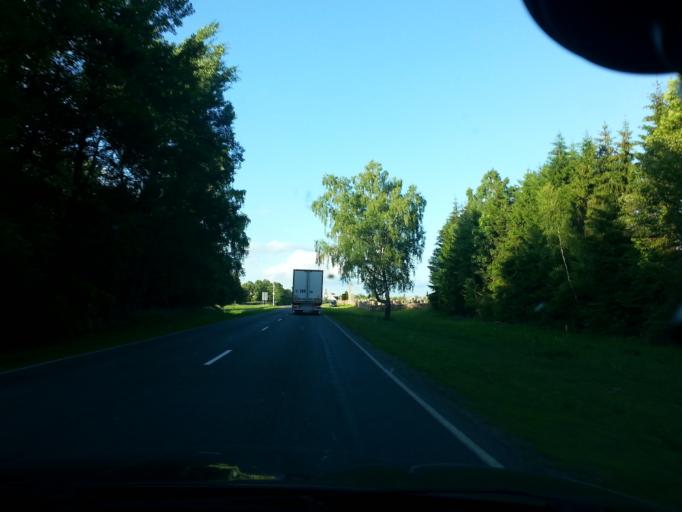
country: BY
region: Minsk
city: Svir
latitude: 54.9121
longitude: 26.4412
